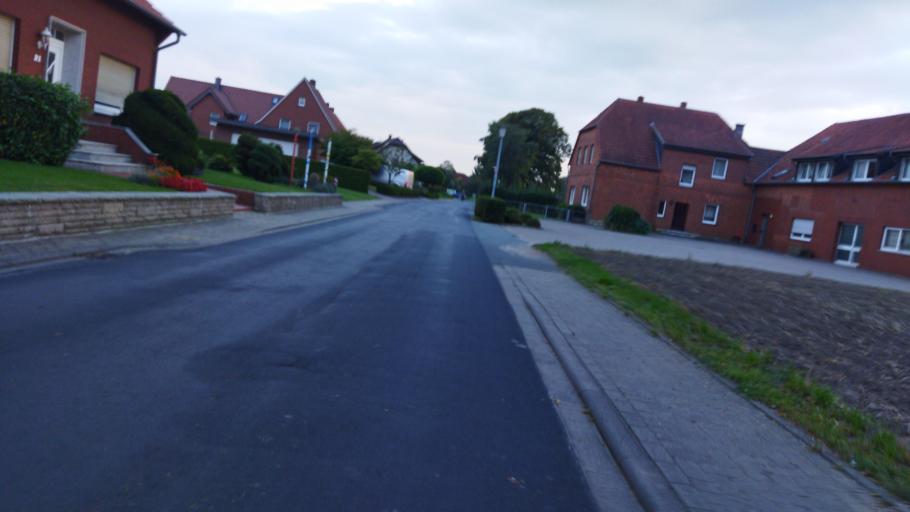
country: DE
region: Lower Saxony
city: Bad Iburg
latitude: 52.1418
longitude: 8.0531
